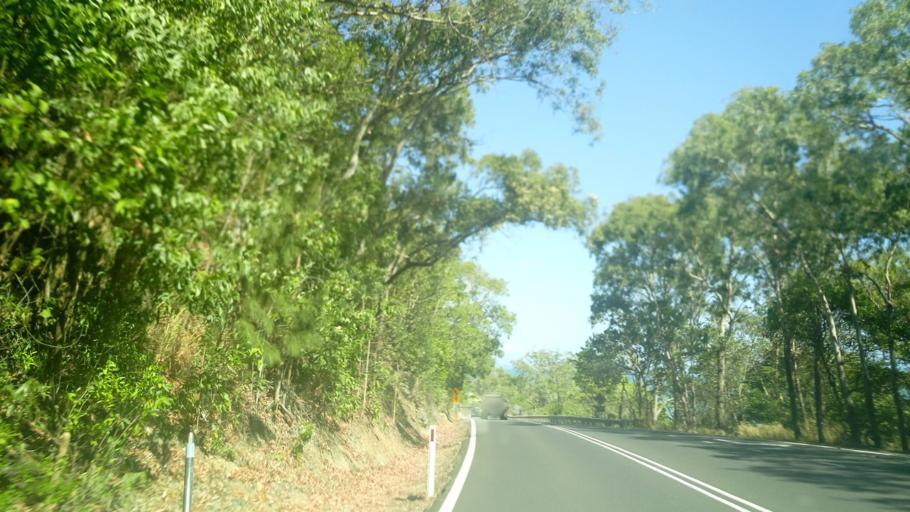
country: AU
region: Queensland
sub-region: Cairns
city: Palm Cove
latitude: -16.7372
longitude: 145.6636
